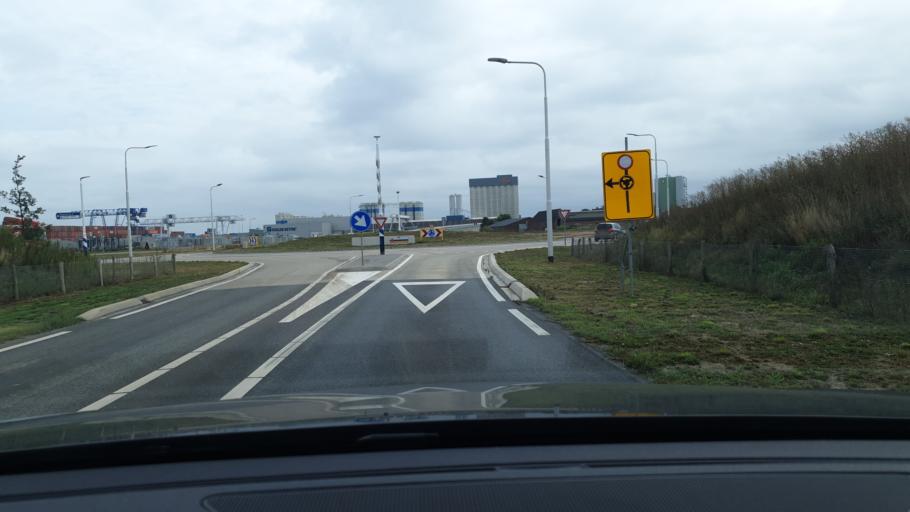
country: NL
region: Limburg
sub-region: Gemeente Bergen
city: Wellerlooi
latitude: 51.5398
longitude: 6.0705
